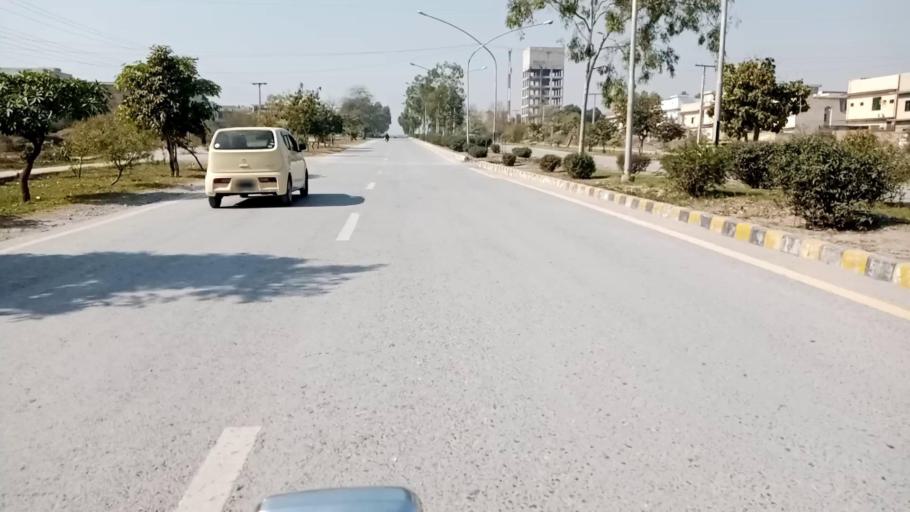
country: PK
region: Khyber Pakhtunkhwa
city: Peshawar
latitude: 33.9564
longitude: 71.4231
